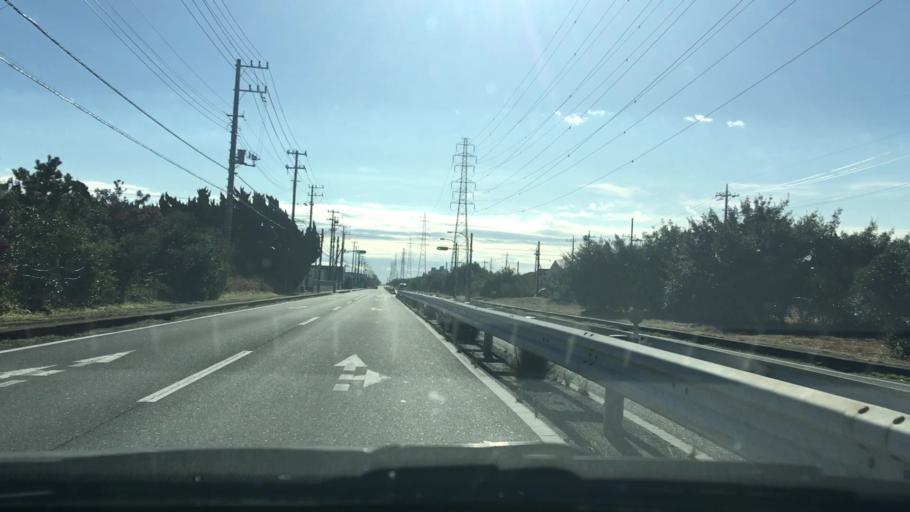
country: JP
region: Chiba
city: Omigawa
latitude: 35.8712
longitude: 140.7225
